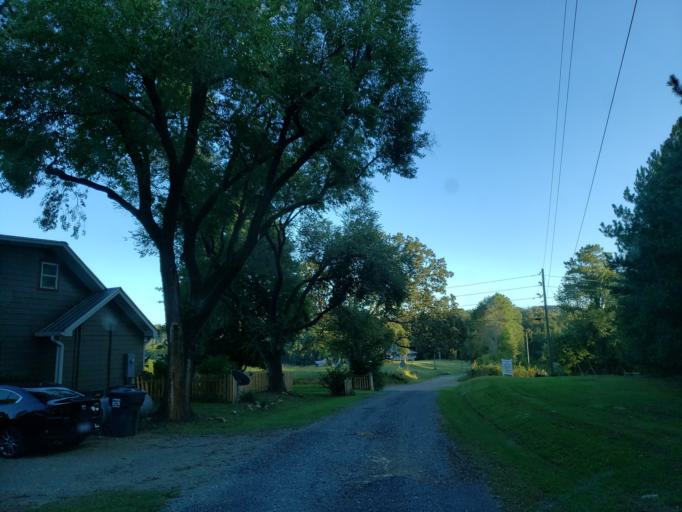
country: US
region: Georgia
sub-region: Bartow County
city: Rydal
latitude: 34.3940
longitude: -84.6451
